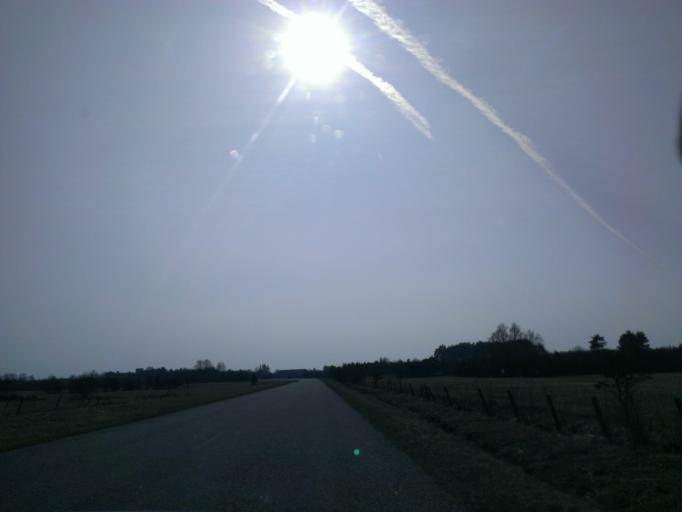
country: EE
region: Saare
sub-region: Orissaare vald
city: Orissaare
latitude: 58.5214
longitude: 23.1075
